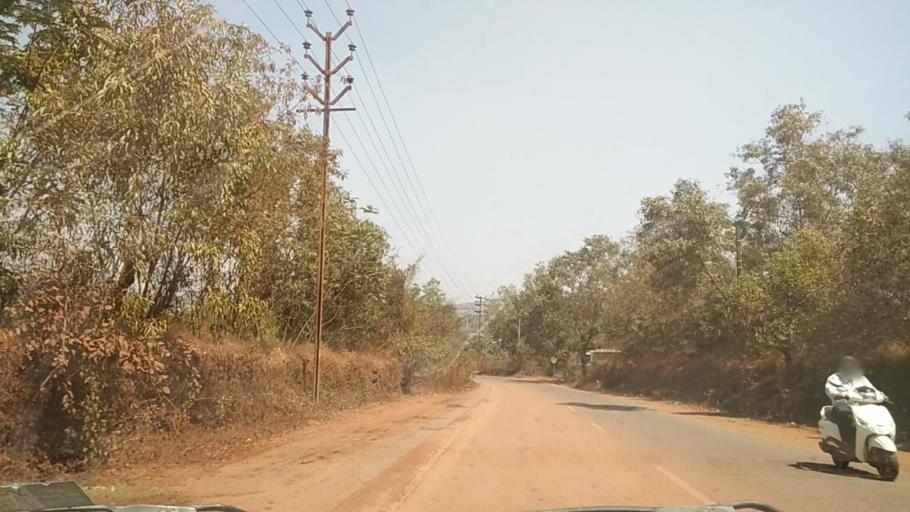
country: IN
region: Goa
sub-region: North Goa
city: Dicholi
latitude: 15.5845
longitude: 73.9414
